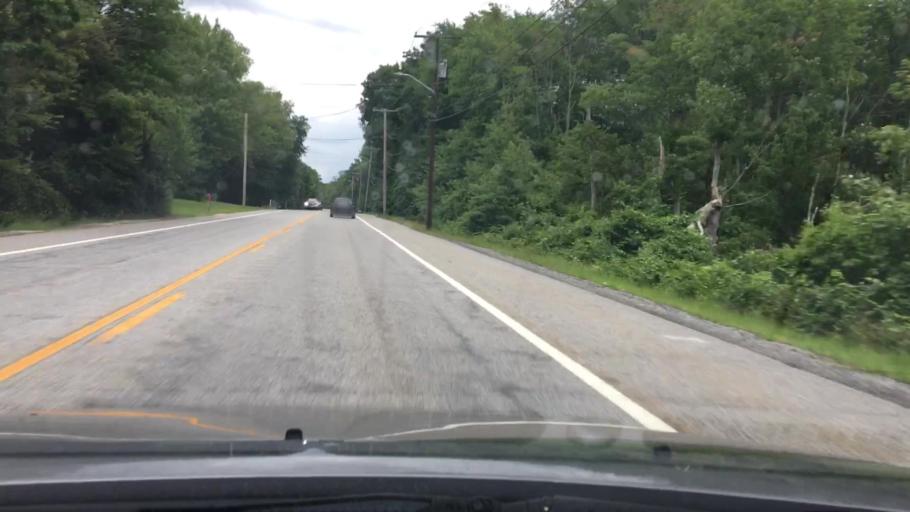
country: US
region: Rhode Island
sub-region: Providence County
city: Cumberland Hill
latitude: 42.0108
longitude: -71.4446
